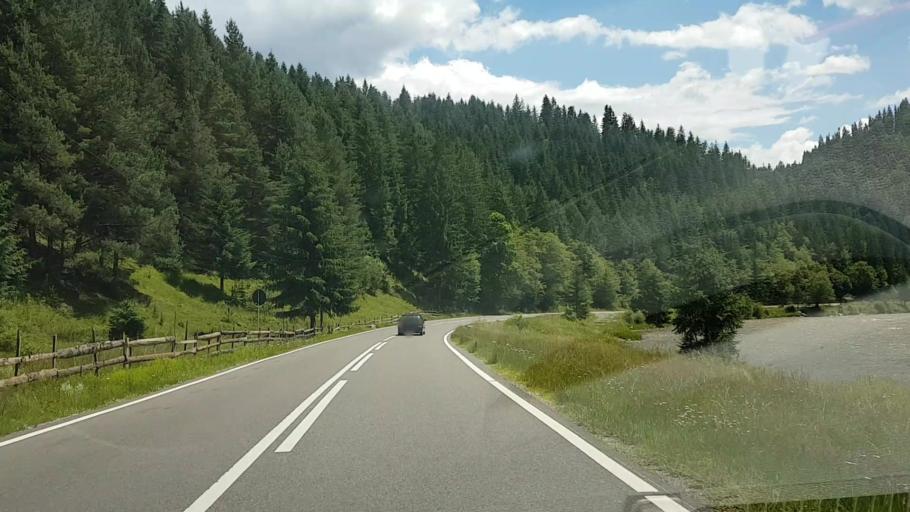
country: RO
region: Suceava
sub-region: Comuna Brosteni
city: Brosteni
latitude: 47.2625
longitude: 25.6667
